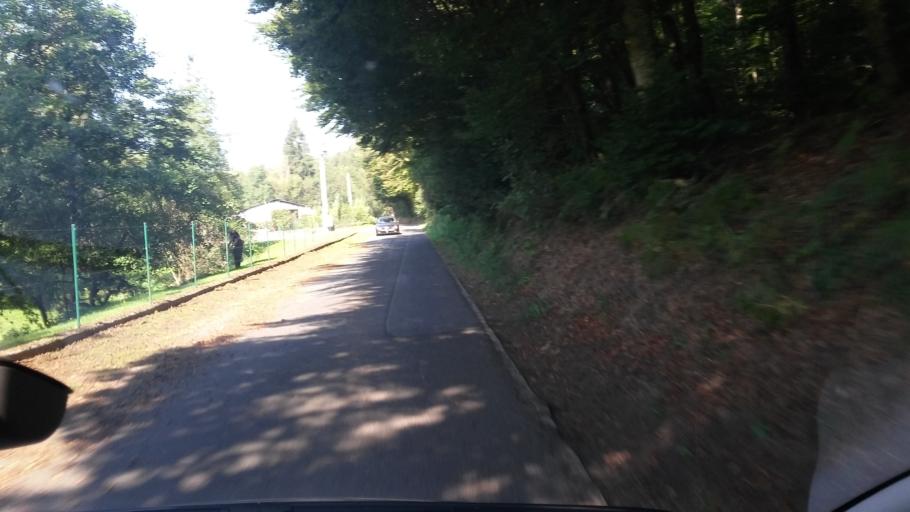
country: LU
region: Luxembourg
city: Eischen
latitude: 49.7007
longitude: 5.8570
